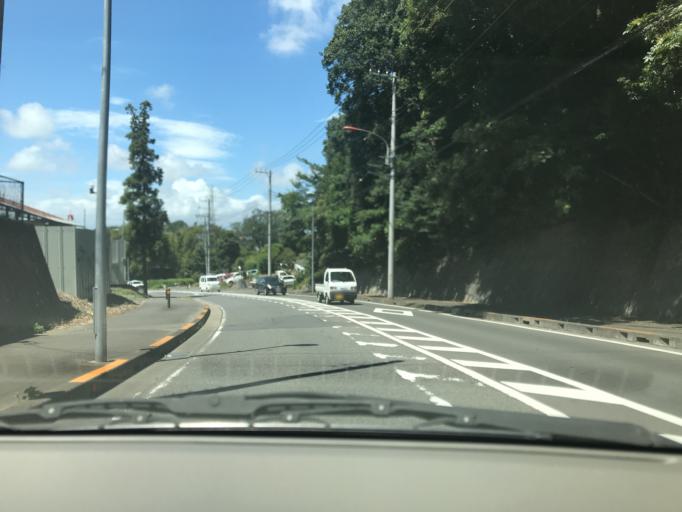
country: JP
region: Kanagawa
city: Fujisawa
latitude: 35.3695
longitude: 139.4581
